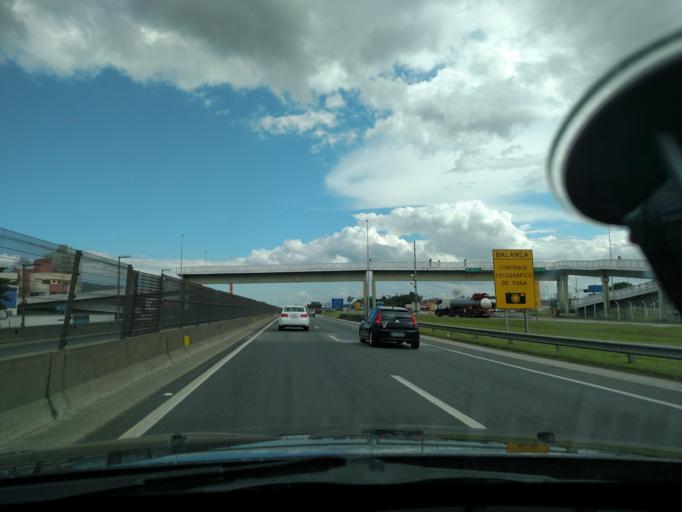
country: BR
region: Santa Catarina
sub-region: Itapema
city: Itapema
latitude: -27.1239
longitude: -48.6095
